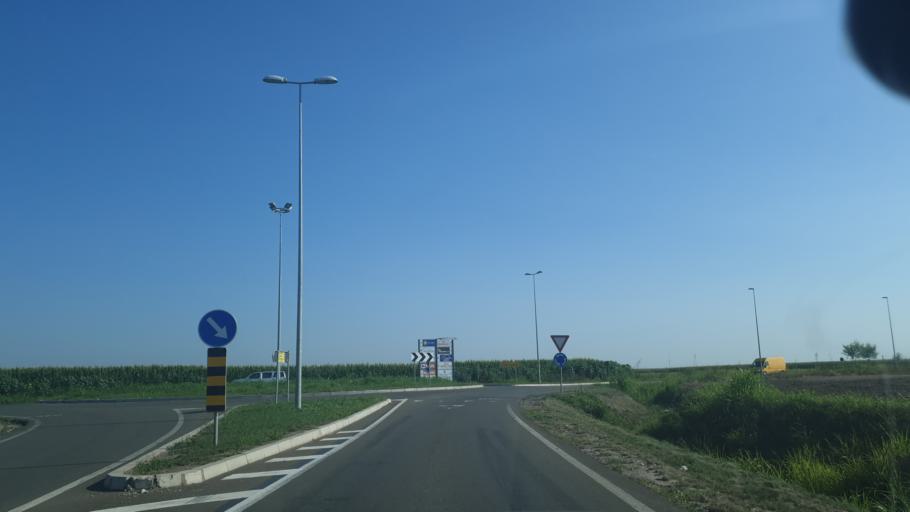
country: RS
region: Autonomna Pokrajina Vojvodina
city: Nova Pazova
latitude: 44.9684
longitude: 20.2421
